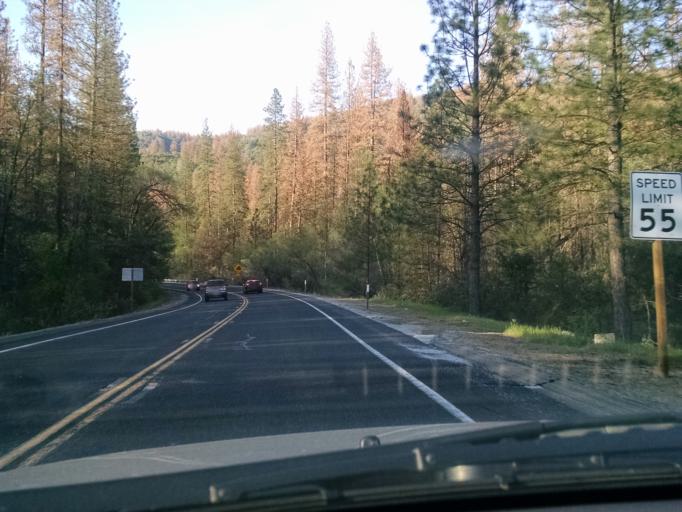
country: US
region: California
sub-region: Madera County
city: Ahwahnee
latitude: 37.4230
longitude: -119.7247
